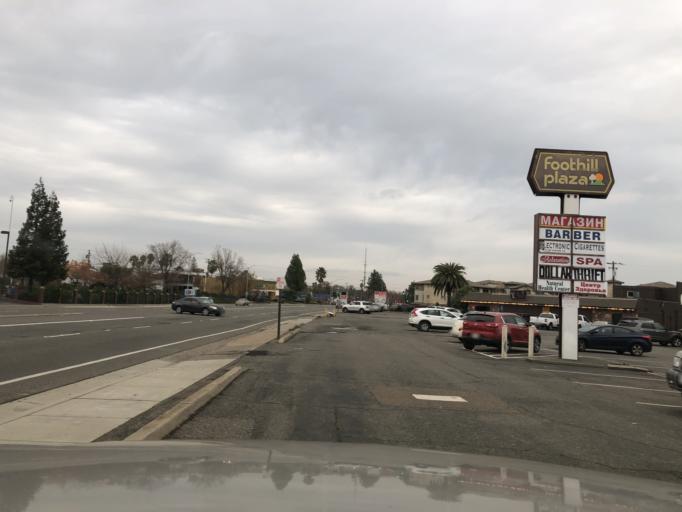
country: US
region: California
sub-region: Sacramento County
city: Foothill Farms
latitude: 38.6663
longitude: -121.3402
